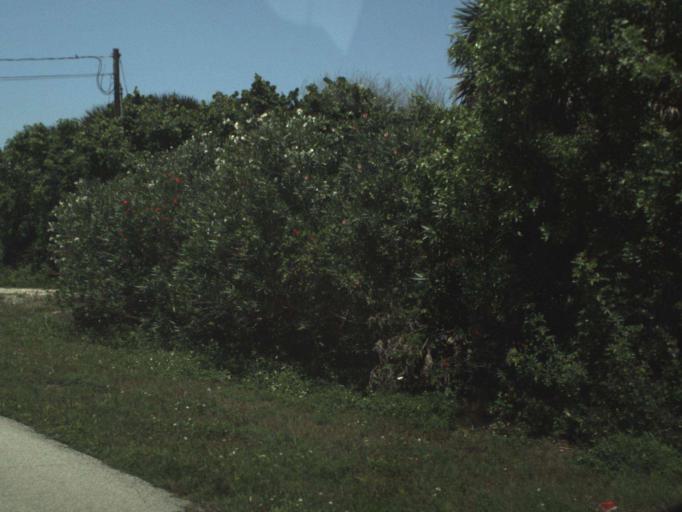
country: US
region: Florida
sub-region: Brevard County
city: Micco
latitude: 27.8974
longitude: -80.4689
